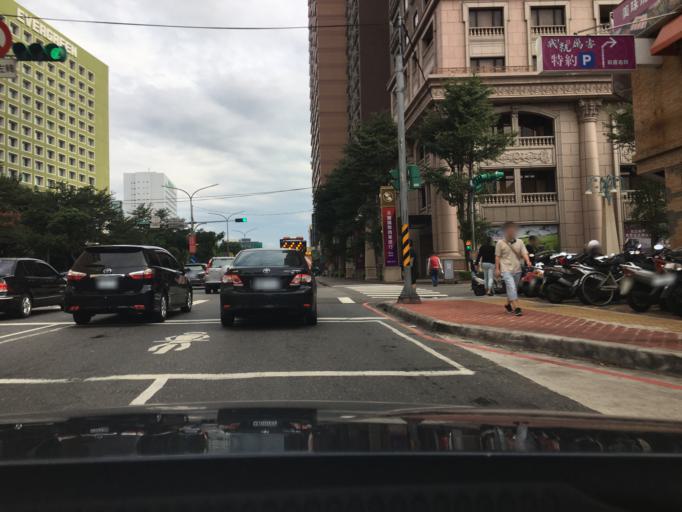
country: TW
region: Taiwan
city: Taoyuan City
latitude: 25.0433
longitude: 121.2944
